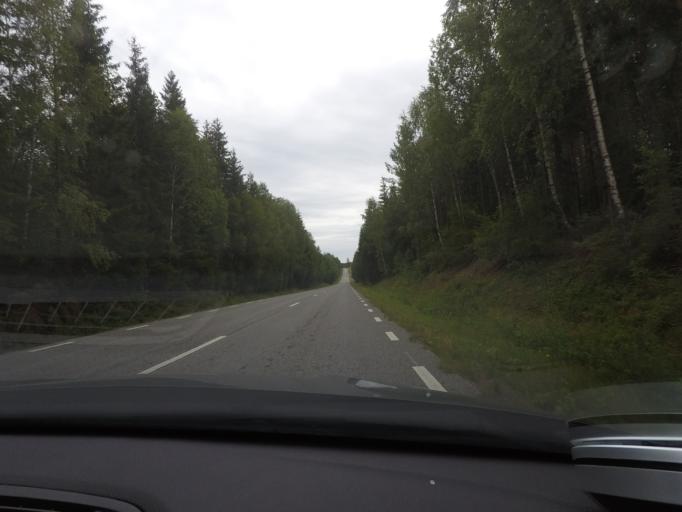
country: SE
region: Blekinge
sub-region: Olofstroms Kommun
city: Olofstroem
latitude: 56.4484
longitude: 14.5456
